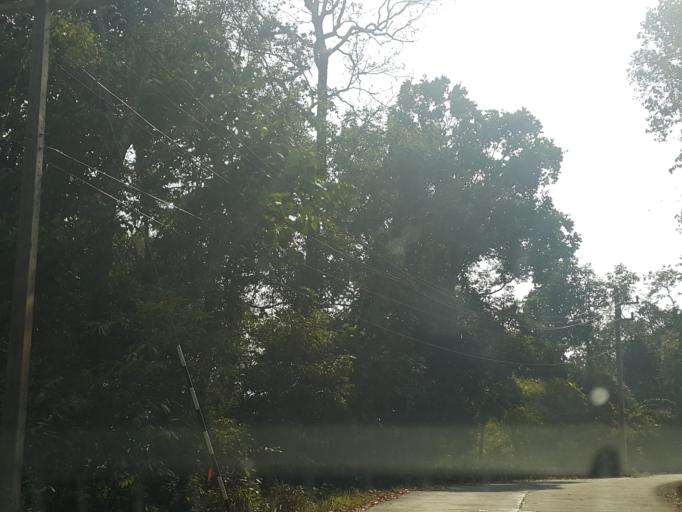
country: TH
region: Chiang Mai
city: Samoeng
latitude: 19.0261
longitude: 98.7766
